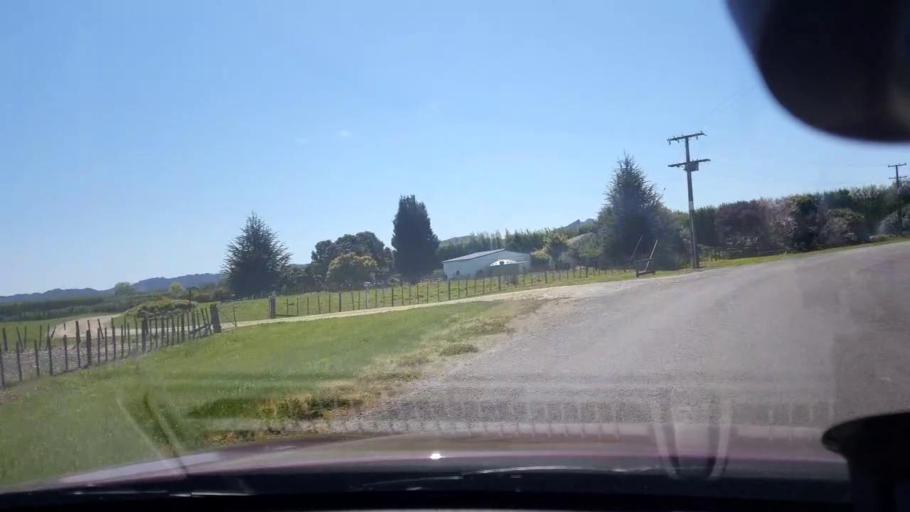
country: NZ
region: Gisborne
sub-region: Gisborne District
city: Gisborne
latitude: -38.6366
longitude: 177.9411
